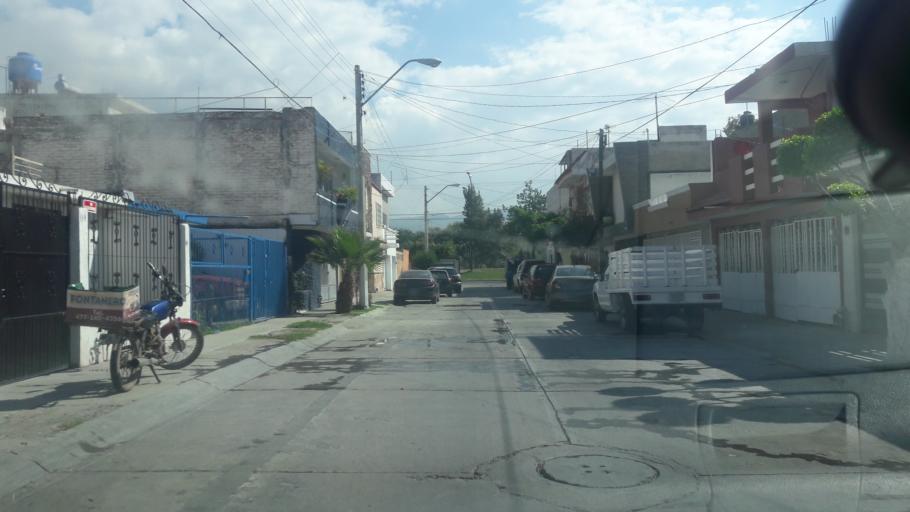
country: MX
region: Guanajuato
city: Leon
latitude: 21.1790
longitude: -101.6650
